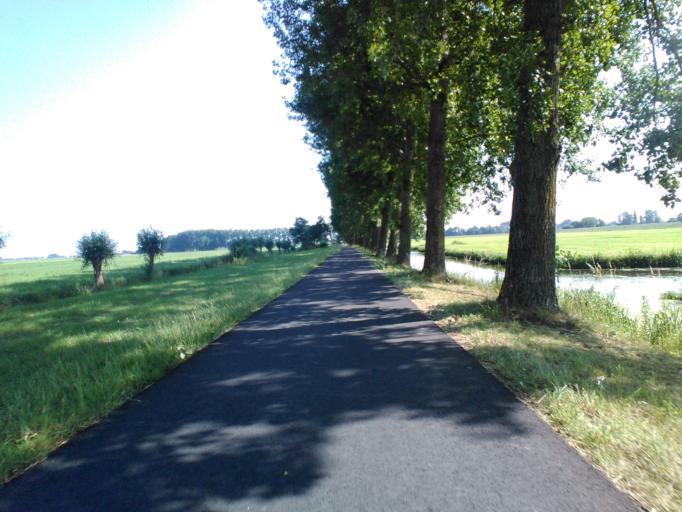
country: NL
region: South Holland
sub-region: Gemeente Alphen aan den Rijn
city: Alphen aan den Rijn
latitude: 52.1539
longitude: 4.6936
